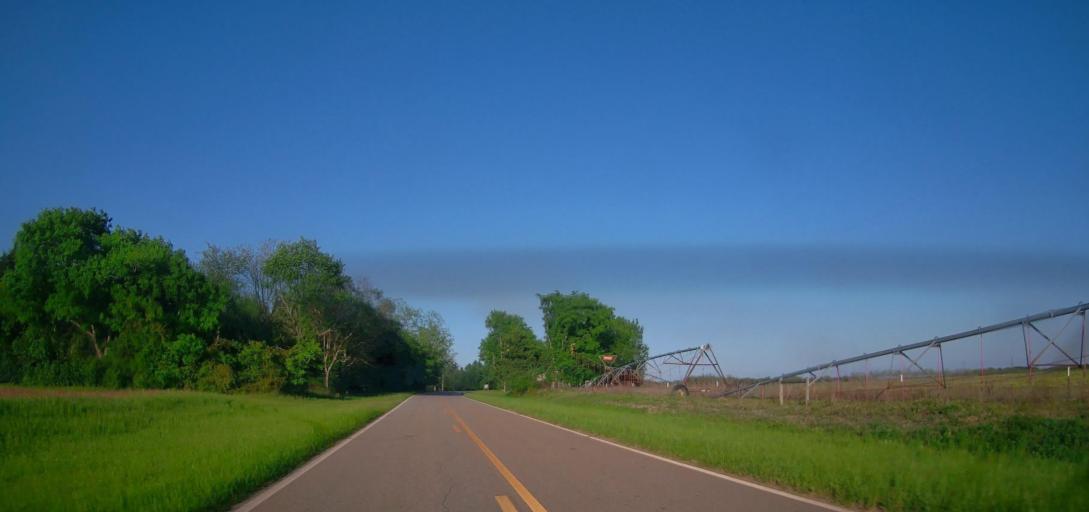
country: US
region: Georgia
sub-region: Macon County
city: Oglethorpe
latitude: 32.3058
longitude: -84.1267
